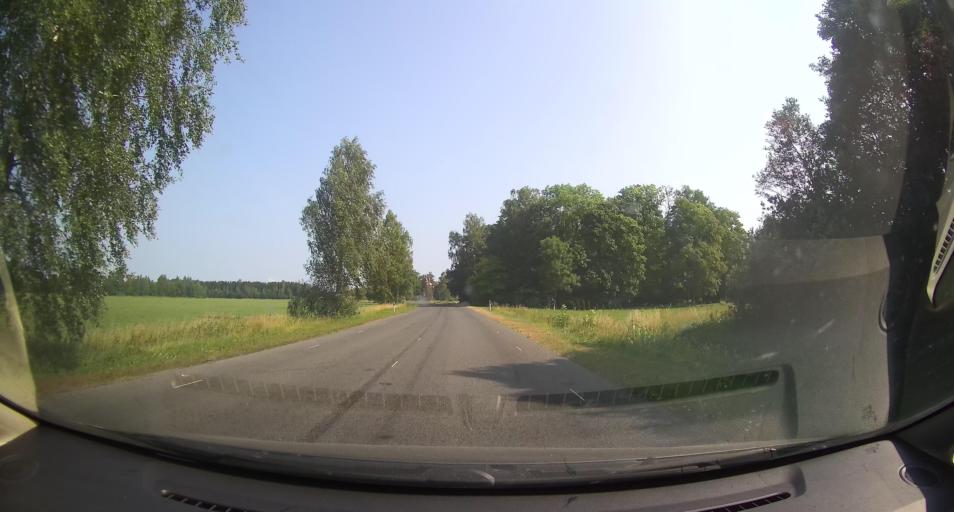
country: EE
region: Paernumaa
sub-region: Audru vald
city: Audru
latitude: 58.4820
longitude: 24.3335
